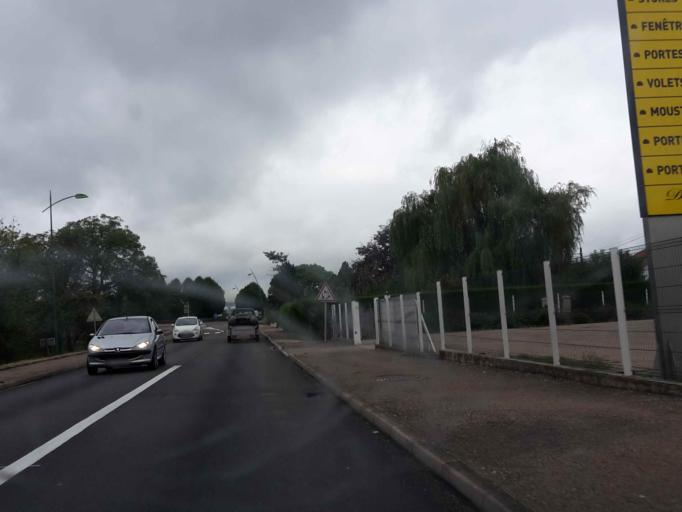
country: FR
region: Franche-Comte
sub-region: Departement du Doubs
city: Novillars
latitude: 47.2744
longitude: 6.1059
